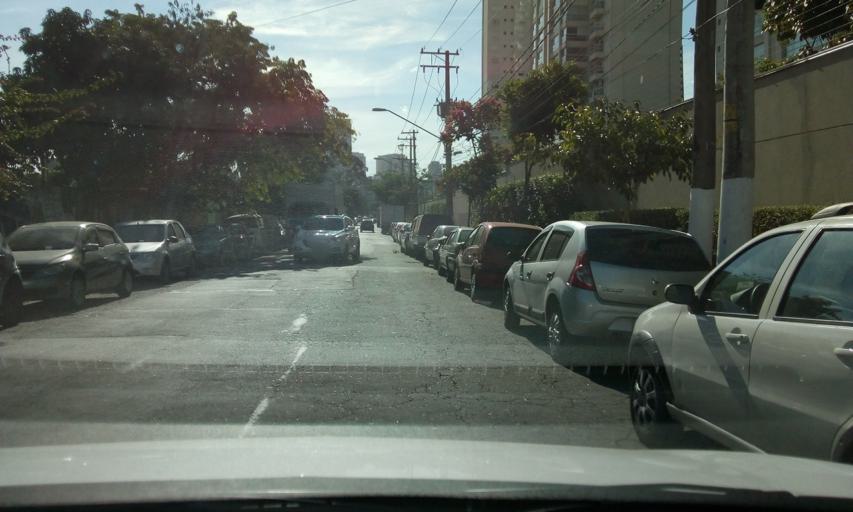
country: BR
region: Sao Paulo
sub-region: Osasco
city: Osasco
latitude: -23.5341
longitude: -46.7320
